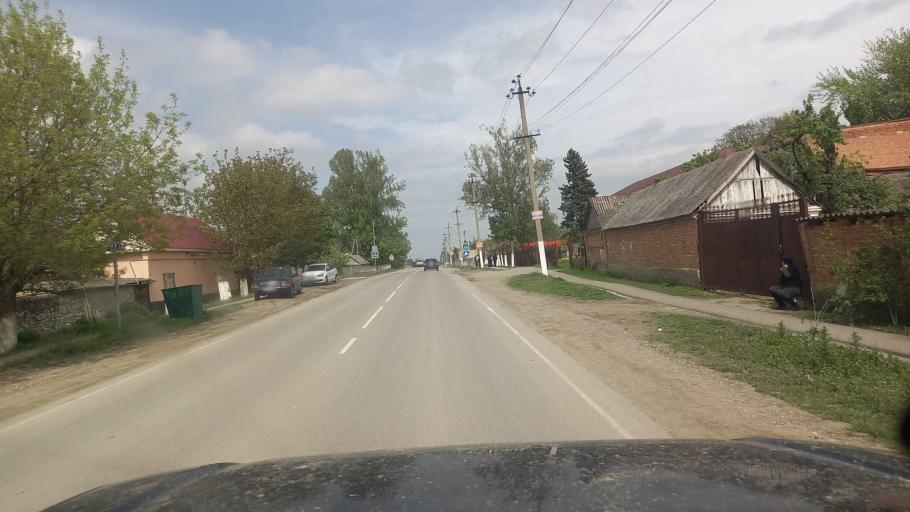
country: RU
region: Kabardino-Balkariya
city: Sarmakovo
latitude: 43.7349
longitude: 43.1770
